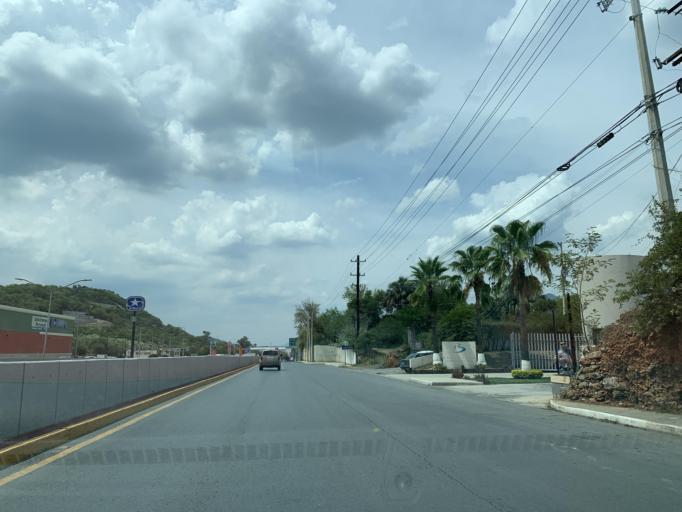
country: MX
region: Nuevo Leon
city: Santiago
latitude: 25.4299
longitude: -100.1507
